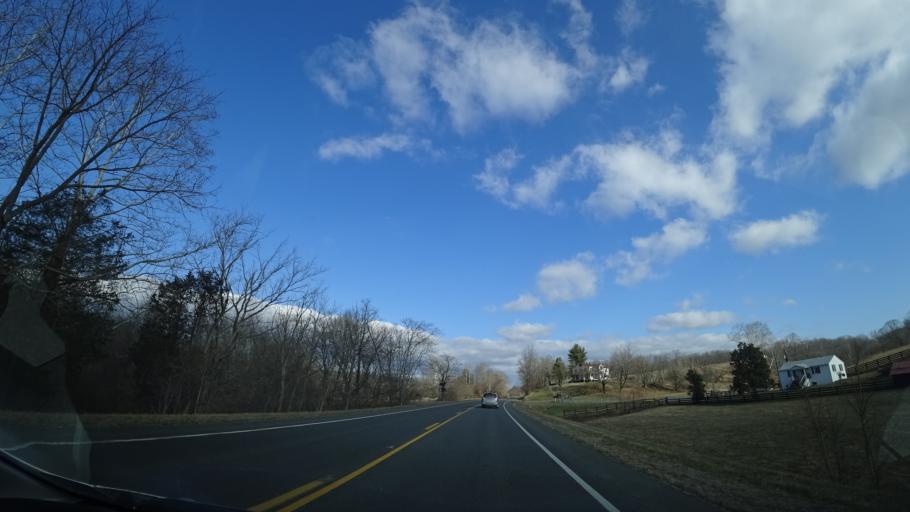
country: US
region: Virginia
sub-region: Fauquier County
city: Marshall
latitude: 38.9268
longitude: -77.9307
